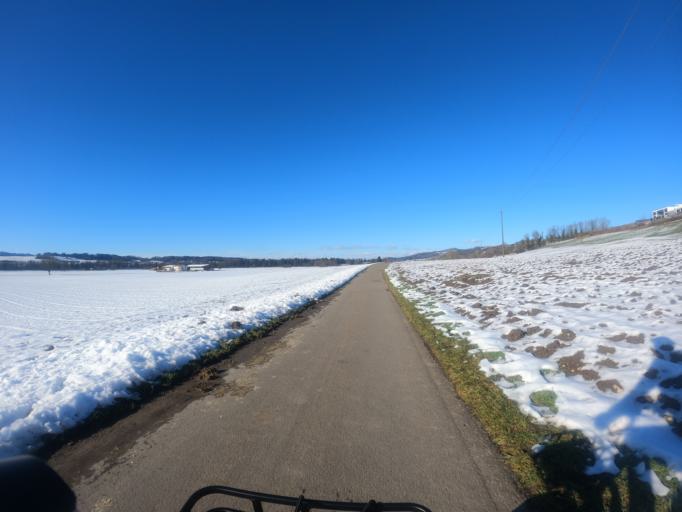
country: CH
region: Aargau
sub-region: Bezirk Bremgarten
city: Jonen
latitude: 47.3002
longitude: 8.3891
